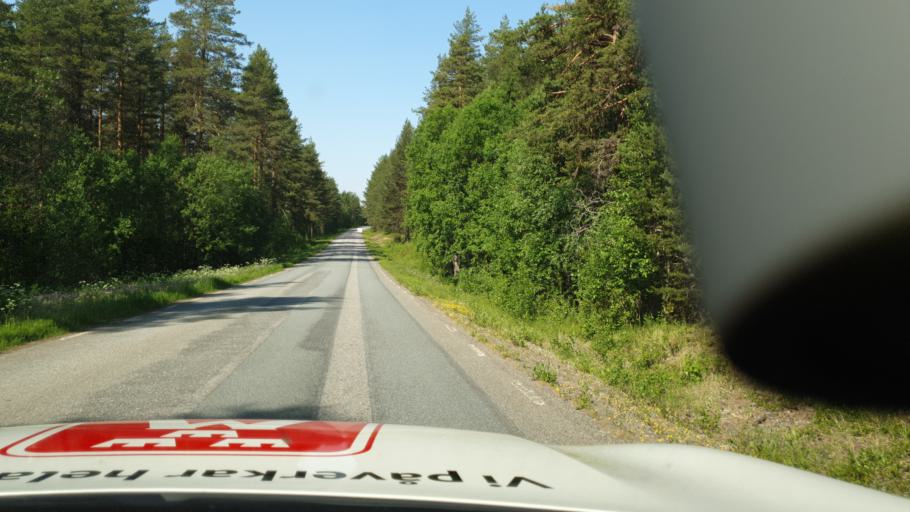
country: SE
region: Vaesterbotten
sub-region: Skelleftea Kommun
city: Langsele
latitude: 64.9420
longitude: 19.9673
